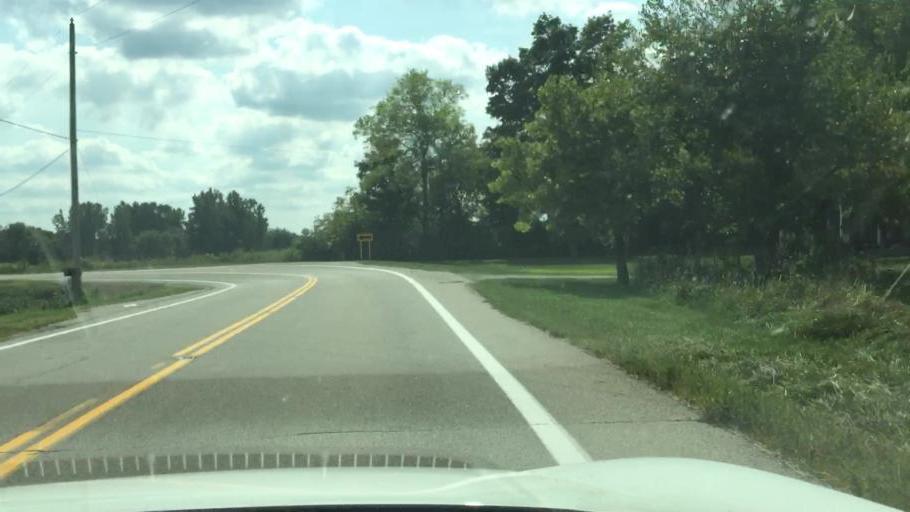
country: US
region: Ohio
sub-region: Champaign County
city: Mechanicsburg
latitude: 40.0869
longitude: -83.5559
